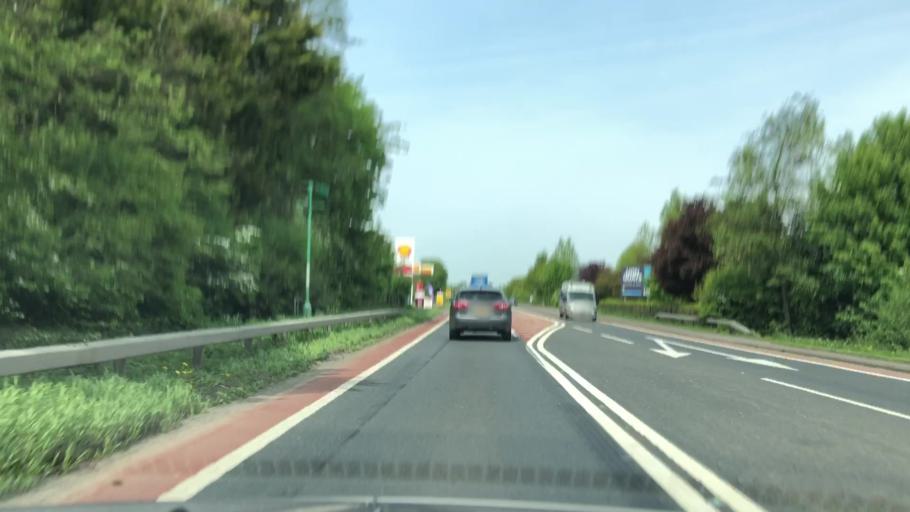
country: GB
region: England
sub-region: Shropshire
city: Gobowen
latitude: 52.9126
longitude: -3.0424
